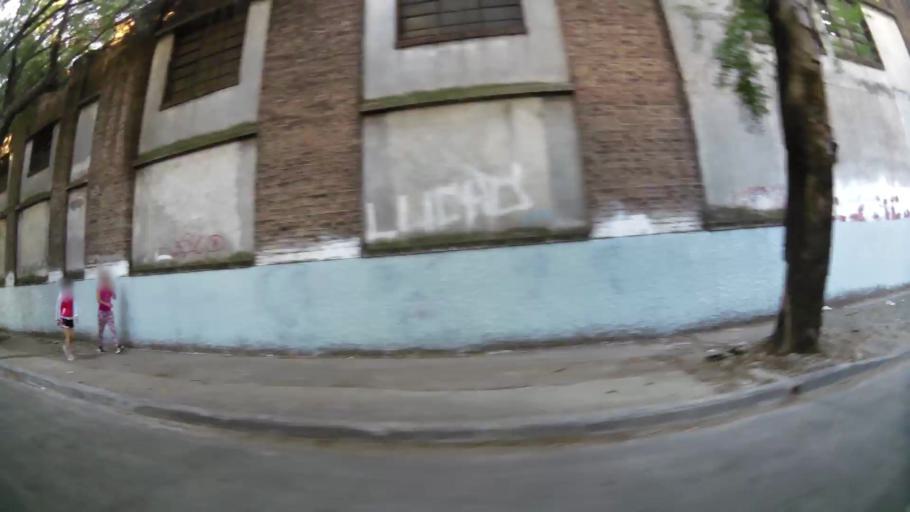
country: AR
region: Buenos Aires
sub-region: Partido de General San Martin
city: General San Martin
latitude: -34.5562
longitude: -58.5232
